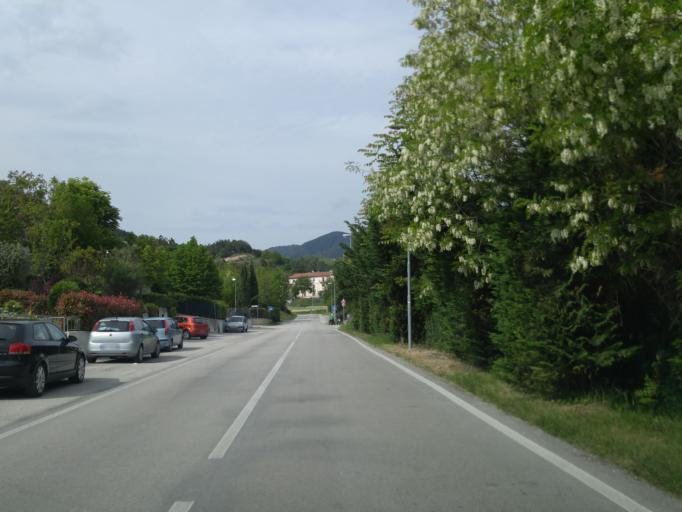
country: IT
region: The Marches
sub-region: Provincia di Pesaro e Urbino
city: Acqualagna
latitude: 43.6260
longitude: 12.6733
